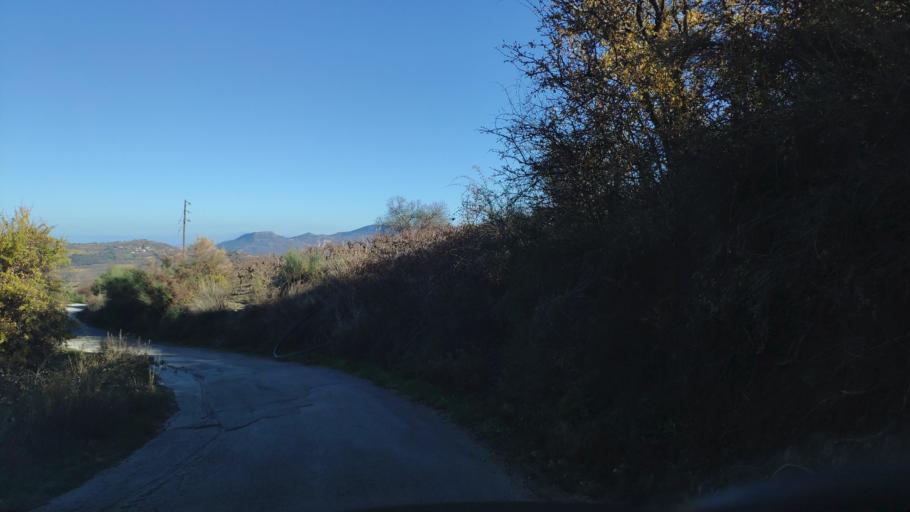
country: GR
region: Peloponnese
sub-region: Nomos Korinthias
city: Xylokastro
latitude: 38.0272
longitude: 22.4925
